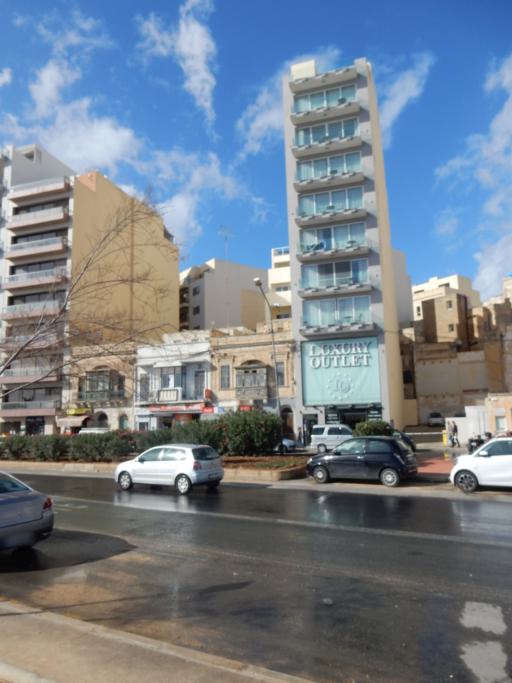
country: MT
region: Tas-Sliema
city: Sliema
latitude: 35.9087
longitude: 14.5034
